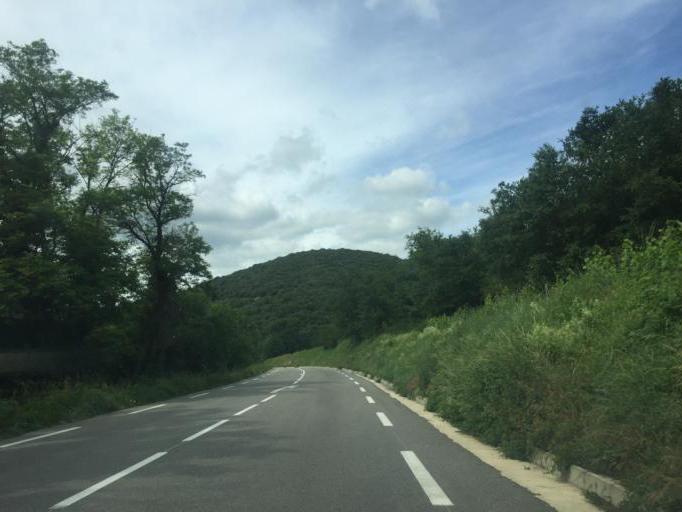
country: FR
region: Rhone-Alpes
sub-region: Departement de l'Ardeche
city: Alba-la-Romaine
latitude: 44.5134
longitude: 4.6275
